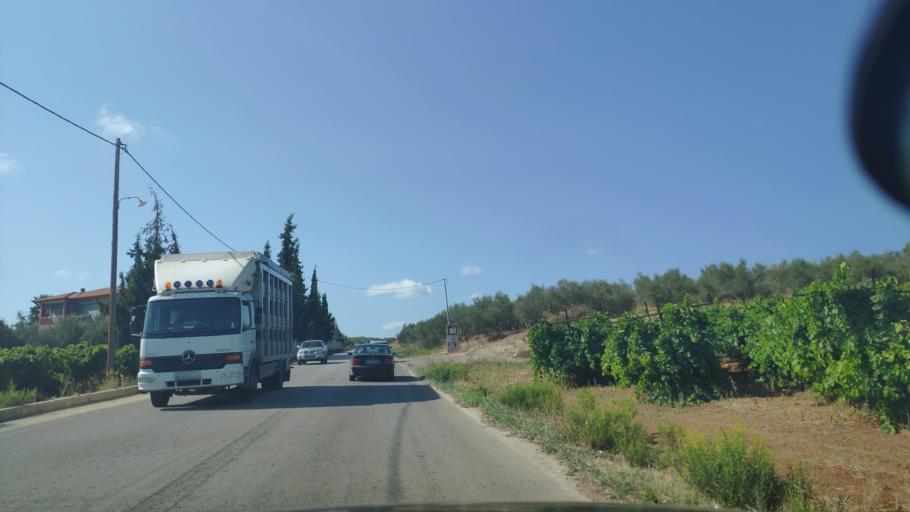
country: GR
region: Peloponnese
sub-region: Nomos Korinthias
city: Moulki
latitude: 37.9932
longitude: 22.7002
